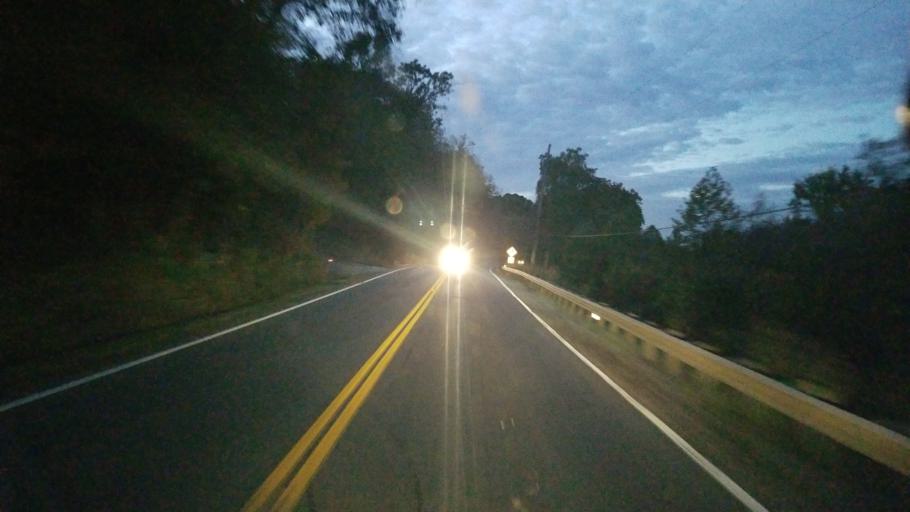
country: US
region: Ohio
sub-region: Scioto County
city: Rosemount
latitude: 38.8250
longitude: -83.0184
